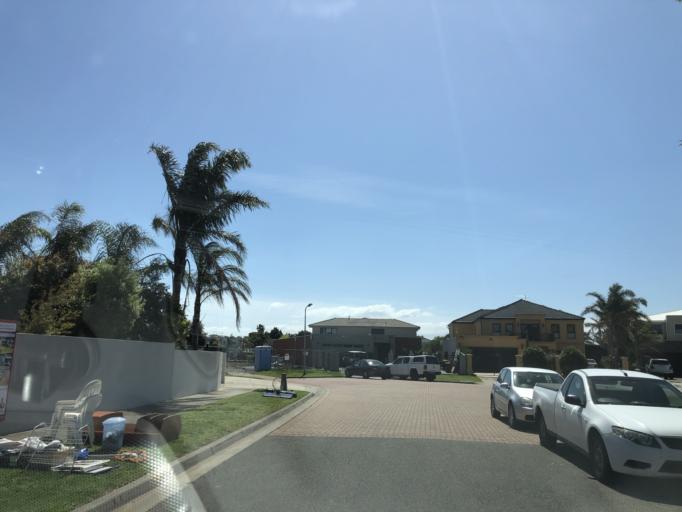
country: AU
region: Victoria
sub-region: Kingston
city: Carrum
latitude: -38.0809
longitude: 145.1409
